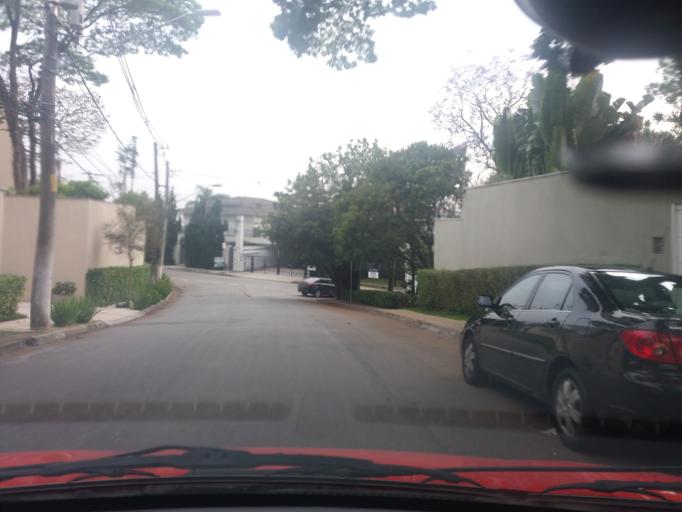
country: BR
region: Sao Paulo
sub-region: Sao Paulo
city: Sao Paulo
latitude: -23.5914
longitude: -46.7108
